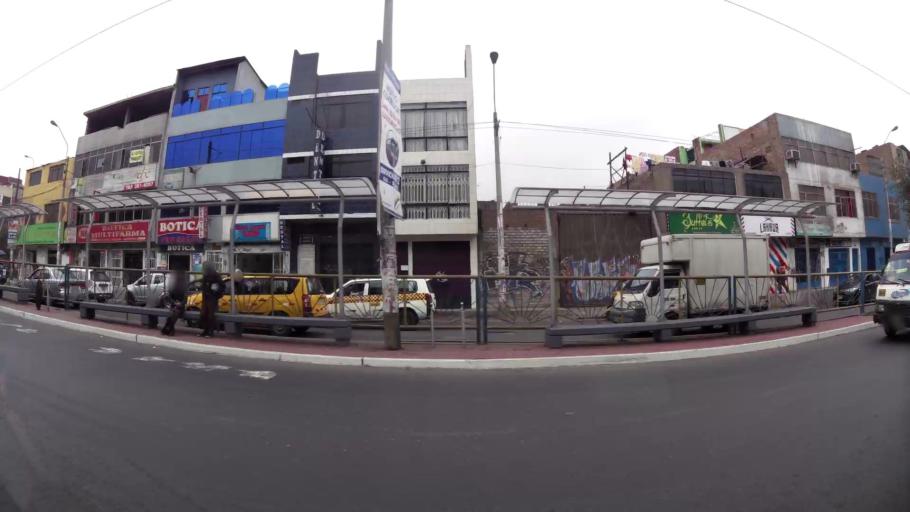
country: PE
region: Lima
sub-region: Lima
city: Independencia
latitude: -11.9904
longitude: -77.0108
